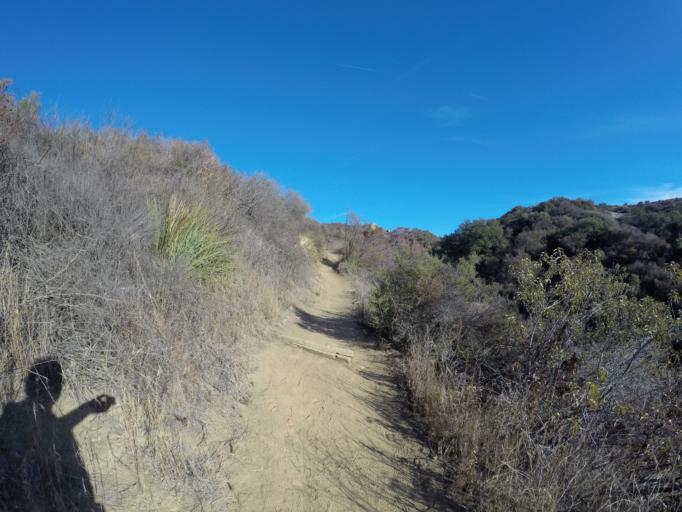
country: US
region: California
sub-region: Los Angeles County
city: Topanga
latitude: 34.1048
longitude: -118.5760
